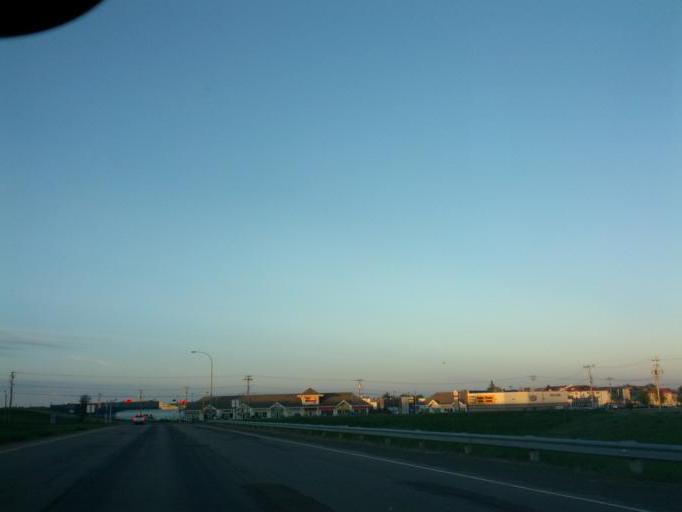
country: CA
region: New Brunswick
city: Moncton
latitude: 46.1117
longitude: -64.8367
